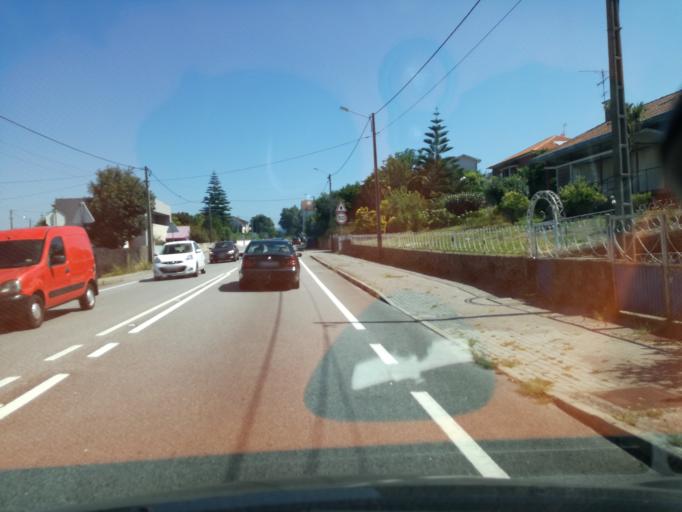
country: ES
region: Galicia
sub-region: Provincia de Pontevedra
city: O Rosal
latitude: 41.9100
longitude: -8.7910
